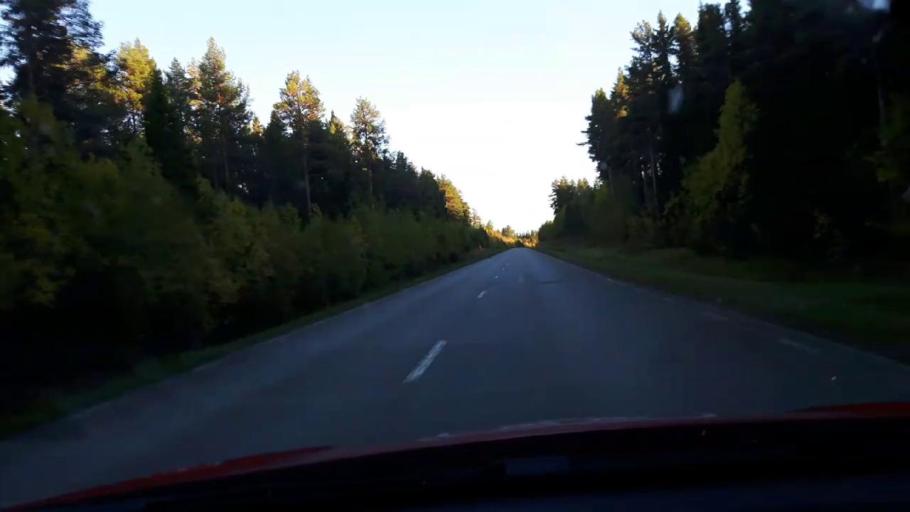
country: SE
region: Jaemtland
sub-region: Krokoms Kommun
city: Krokom
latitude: 63.4410
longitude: 14.4955
